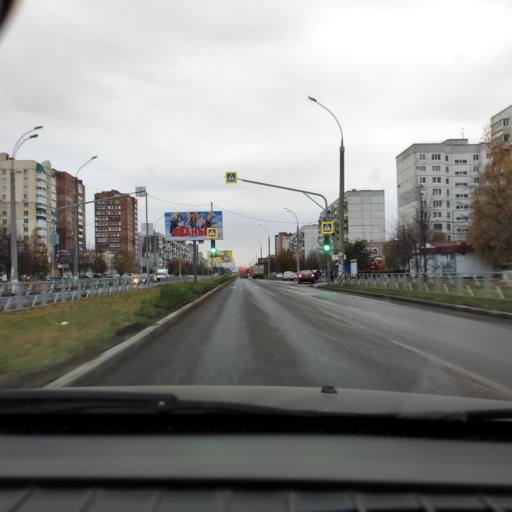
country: RU
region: Samara
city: Tol'yatti
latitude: 53.5476
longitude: 49.3320
